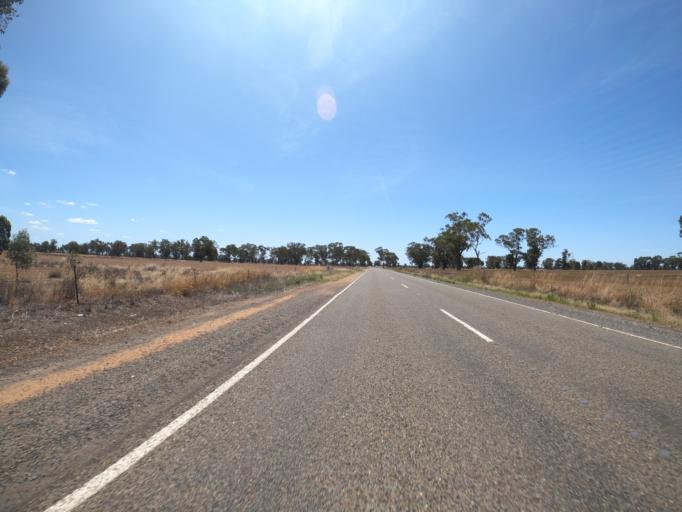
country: AU
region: Victoria
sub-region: Moira
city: Yarrawonga
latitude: -36.1818
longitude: 145.9672
